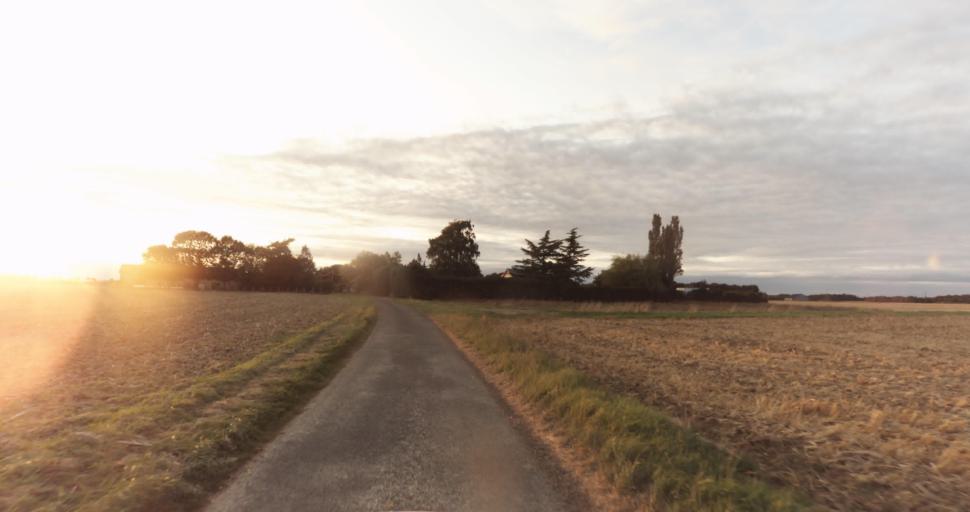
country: FR
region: Haute-Normandie
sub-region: Departement de l'Eure
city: La Madeleine-de-Nonancourt
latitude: 48.8681
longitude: 1.1871
